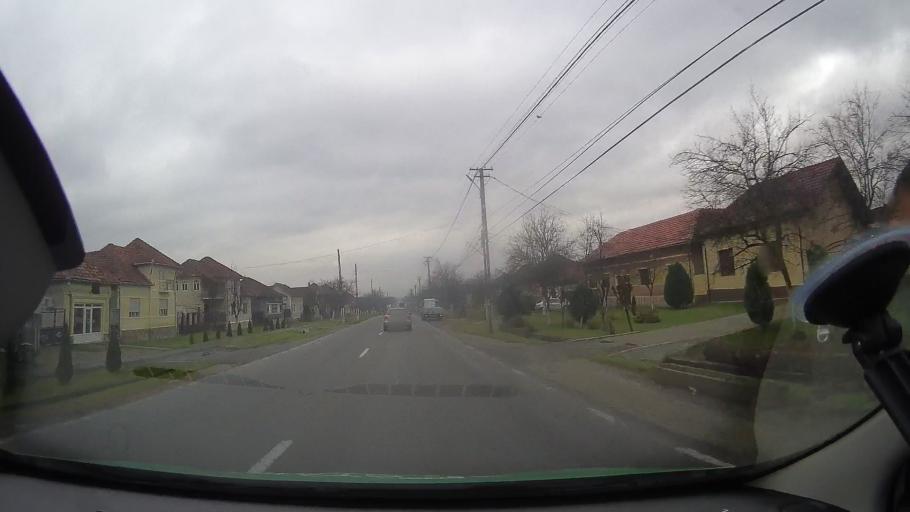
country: RO
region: Arad
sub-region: Comuna Almas
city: Almas
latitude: 46.2841
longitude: 22.2569
